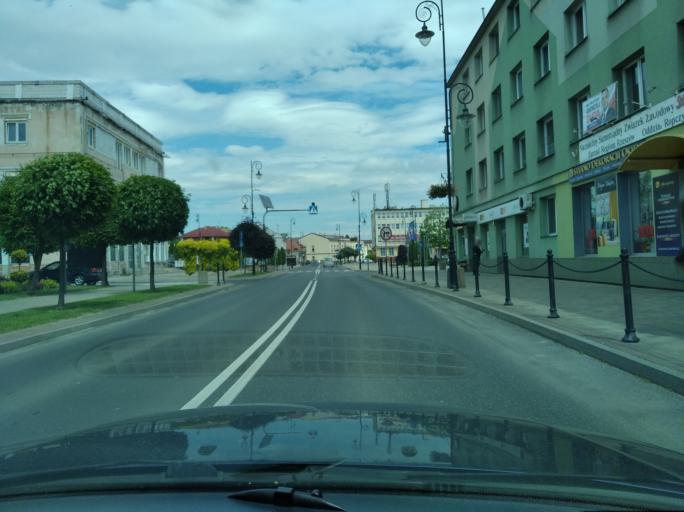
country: PL
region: Subcarpathian Voivodeship
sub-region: Powiat ropczycko-sedziszowski
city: Ropczyce
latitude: 50.0525
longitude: 21.6101
